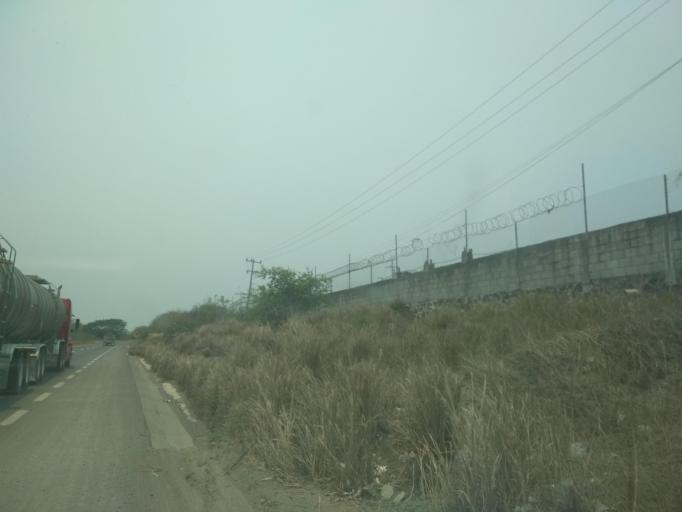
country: MX
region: Veracruz
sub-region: Veracruz
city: Delfino Victoria (Santa Fe)
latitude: 19.2164
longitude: -96.2581
